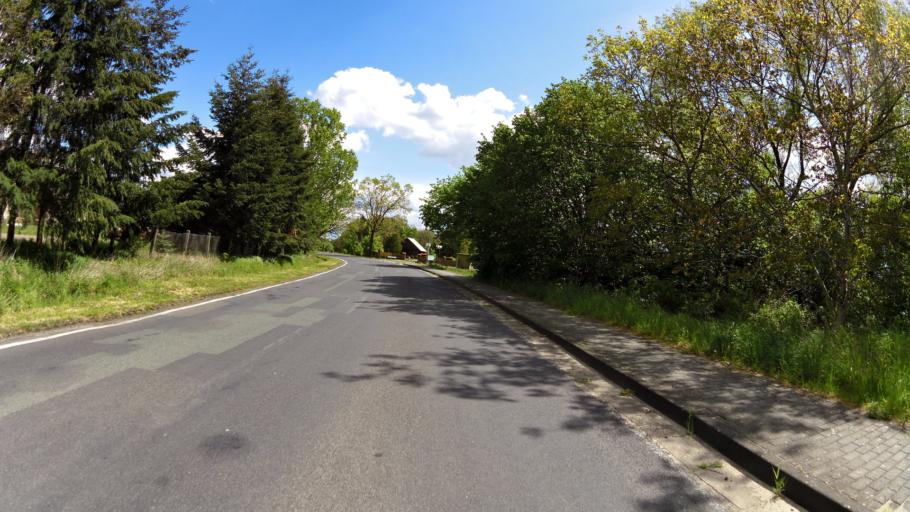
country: DE
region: Brandenburg
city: Wendisch Rietz
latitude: 52.1585
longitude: 14.0210
